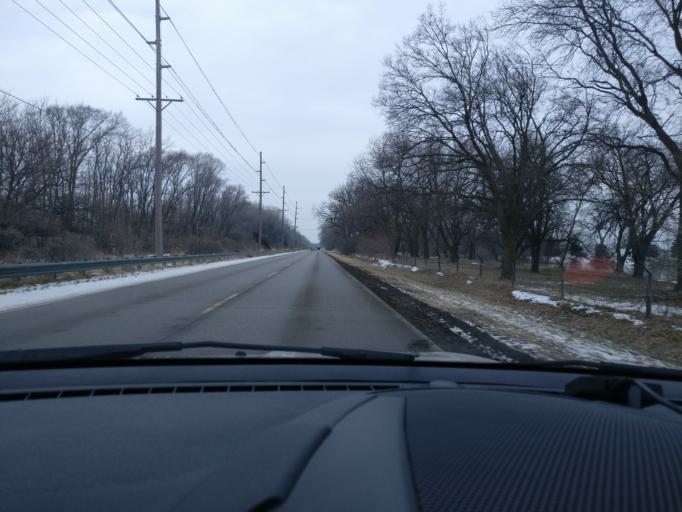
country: US
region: Nebraska
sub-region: Dodge County
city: Fremont
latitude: 41.4420
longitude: -96.5339
